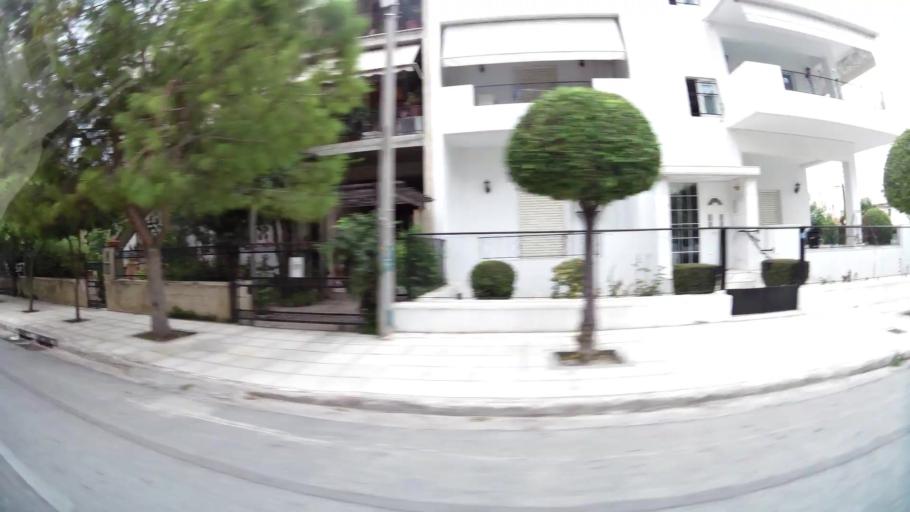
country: GR
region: Attica
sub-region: Nomarchia Athinas
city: Argyroupoli
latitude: 37.9112
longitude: 23.7413
